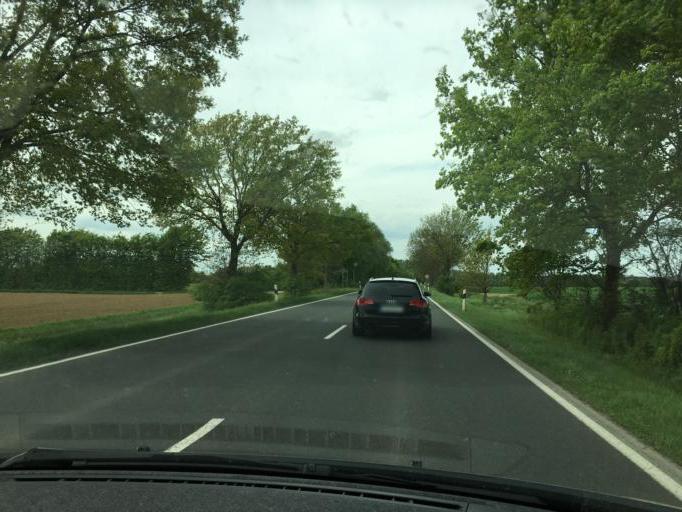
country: DE
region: North Rhine-Westphalia
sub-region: Regierungsbezirk Koln
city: Euskirchen
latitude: 50.6946
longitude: 6.7256
